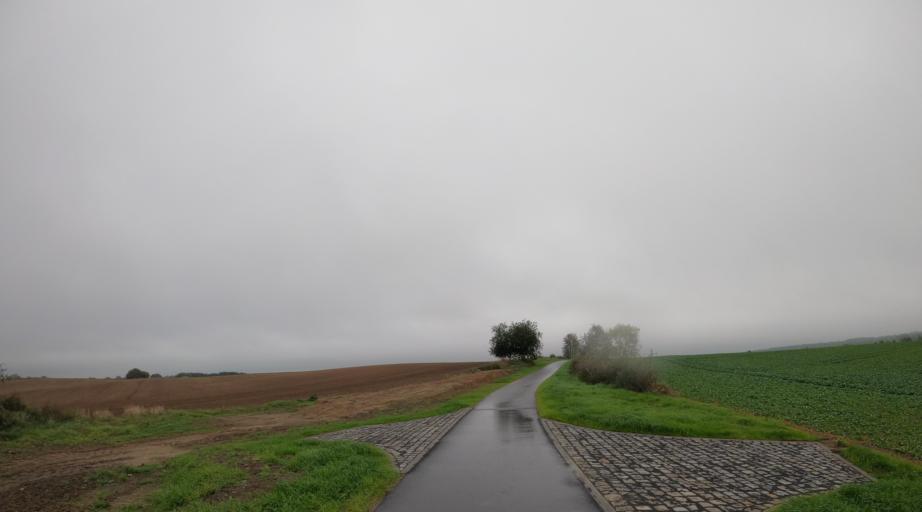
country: PL
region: West Pomeranian Voivodeship
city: Trzcinsko Zdroj
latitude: 52.9249
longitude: 14.7340
